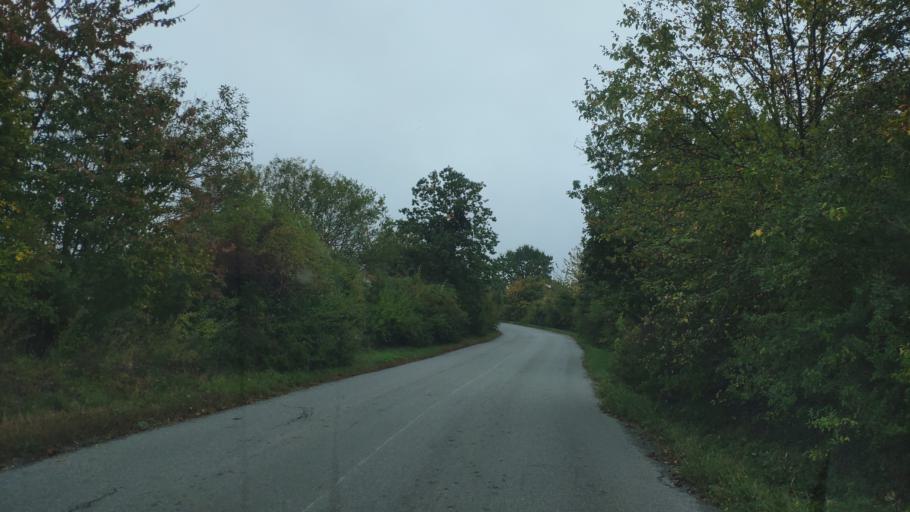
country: SK
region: Kosicky
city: Kosice
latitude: 48.8012
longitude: 21.3941
